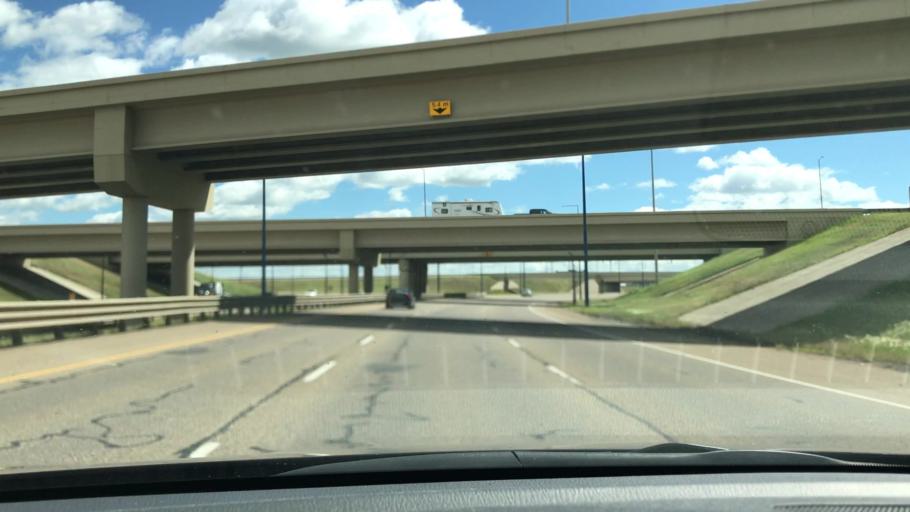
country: CA
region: Alberta
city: Edmonton
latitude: 53.4384
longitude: -113.4910
